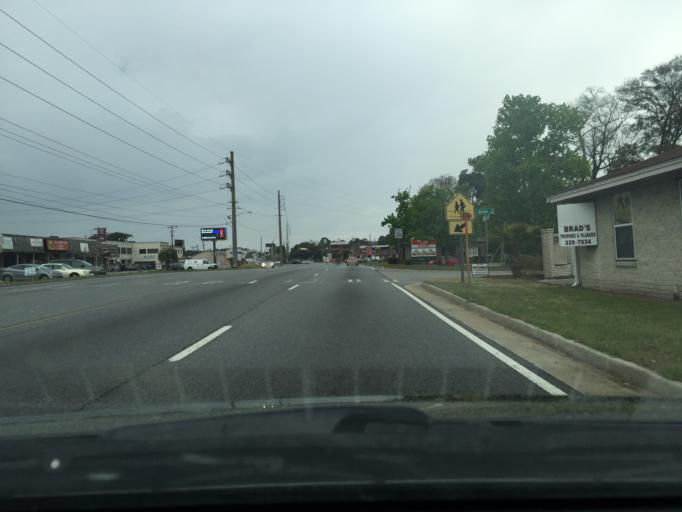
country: US
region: Georgia
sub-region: Chatham County
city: Montgomery
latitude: 31.9979
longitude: -81.1200
